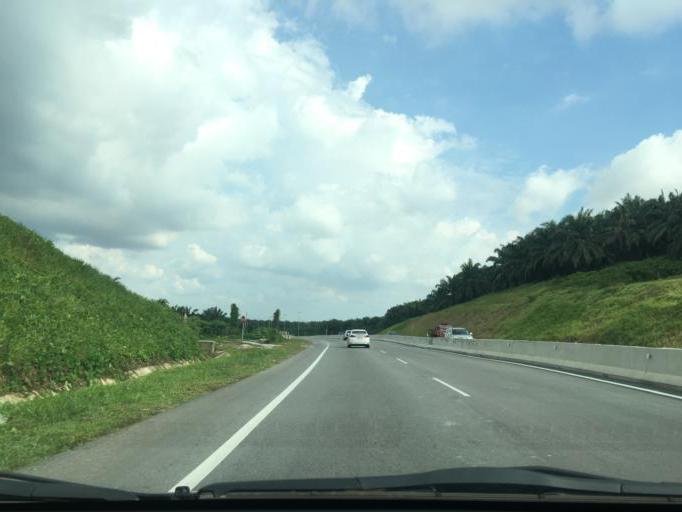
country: MY
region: Selangor
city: Batu Arang
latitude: 3.2883
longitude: 101.4423
